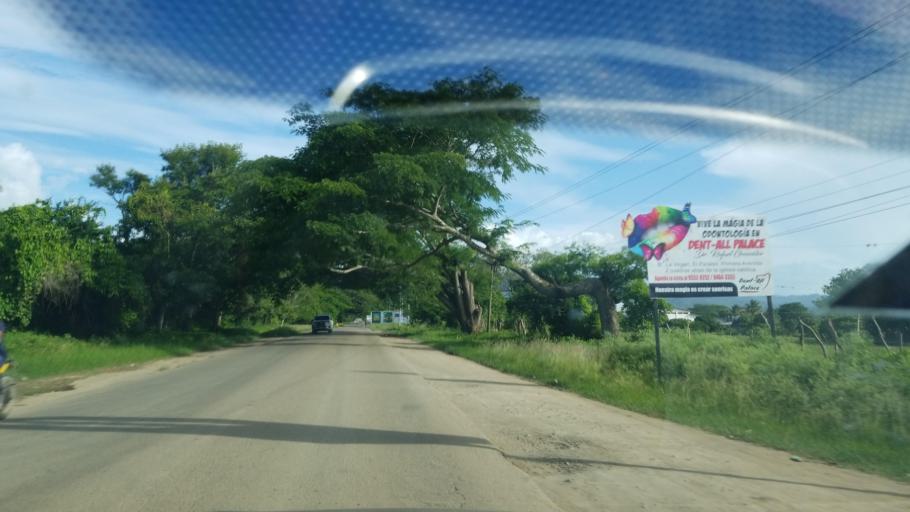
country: HN
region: El Paraiso
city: Cuyali
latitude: 13.8964
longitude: -86.5557
